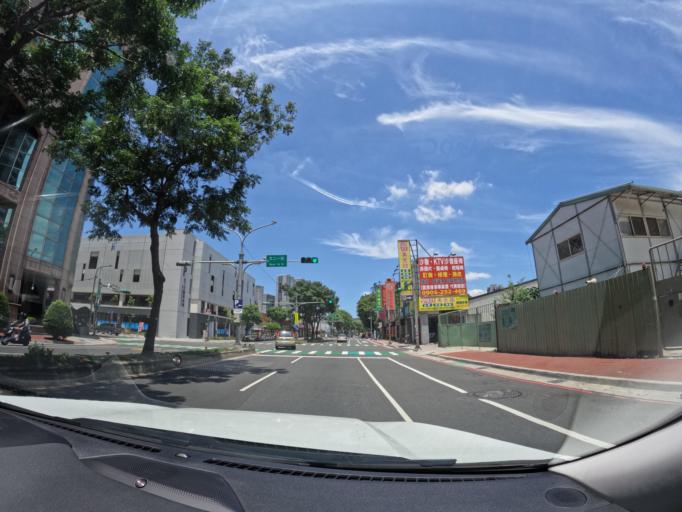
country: TW
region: Taiwan
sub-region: Taoyuan
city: Taoyuan
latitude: 25.0609
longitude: 121.3646
